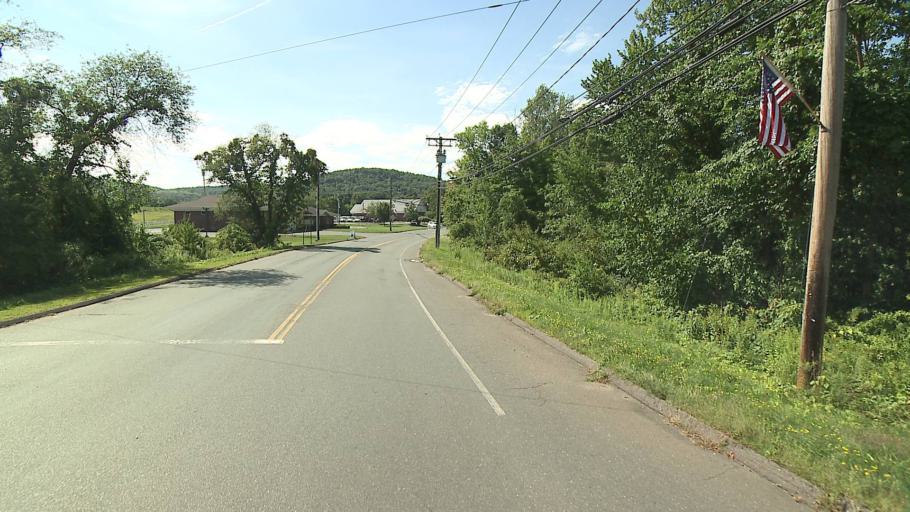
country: US
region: Connecticut
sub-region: Hartford County
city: West Simsbury
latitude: 41.8711
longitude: -72.8524
